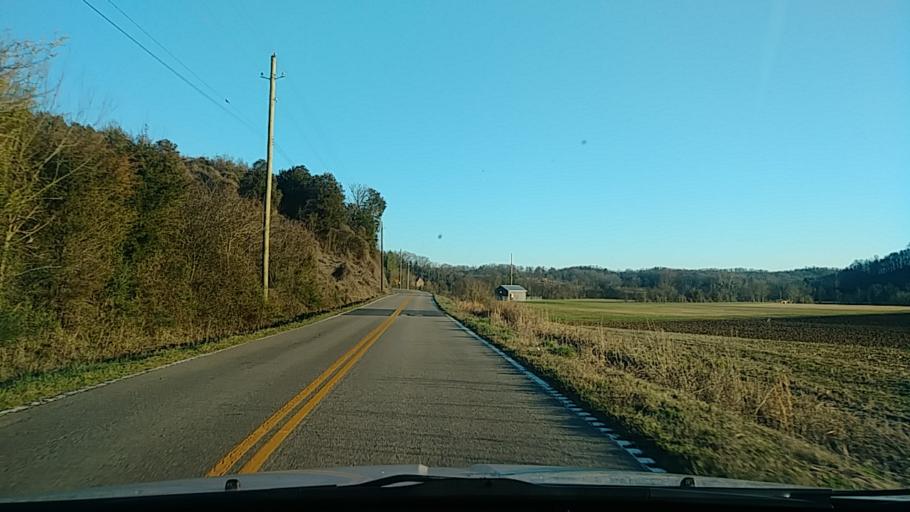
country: US
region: Tennessee
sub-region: Jefferson County
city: White Pine
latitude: 36.1283
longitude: -83.1263
